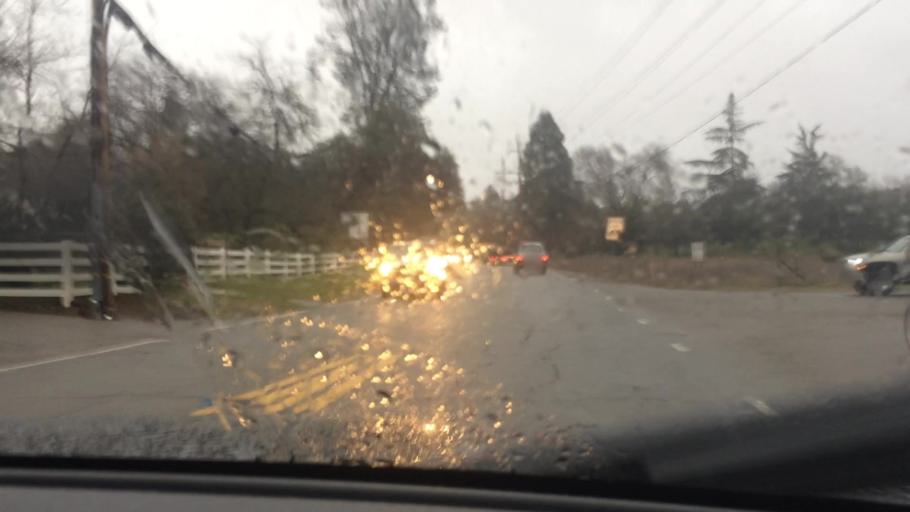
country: US
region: California
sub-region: El Dorado County
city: Deer Park
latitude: 38.6829
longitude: -120.8384
